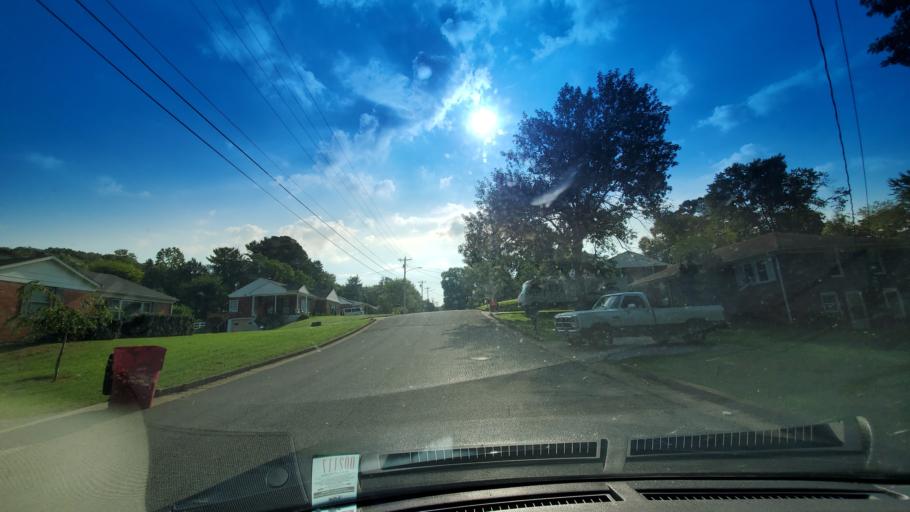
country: US
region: Tennessee
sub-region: Smith County
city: Carthage
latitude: 36.2574
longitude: -85.9446
